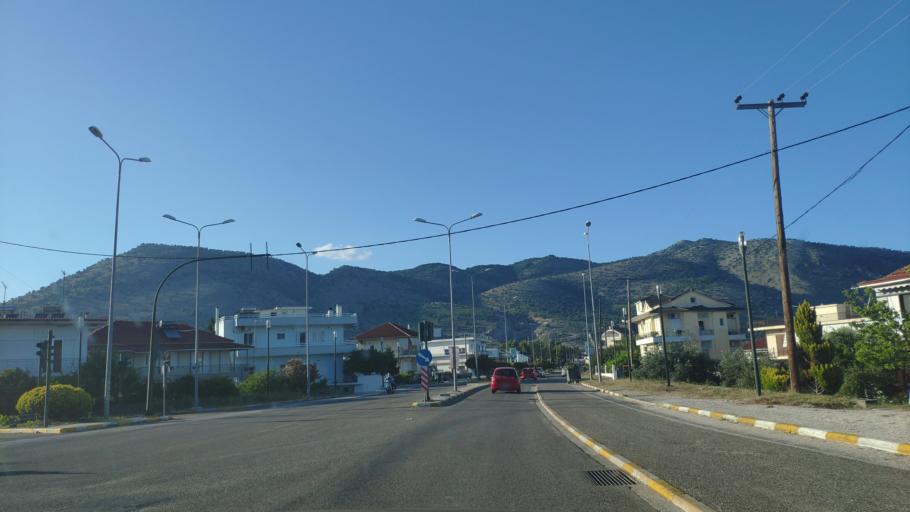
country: GR
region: Epirus
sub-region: Nomos Prevezis
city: Louros
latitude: 39.1599
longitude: 20.7537
